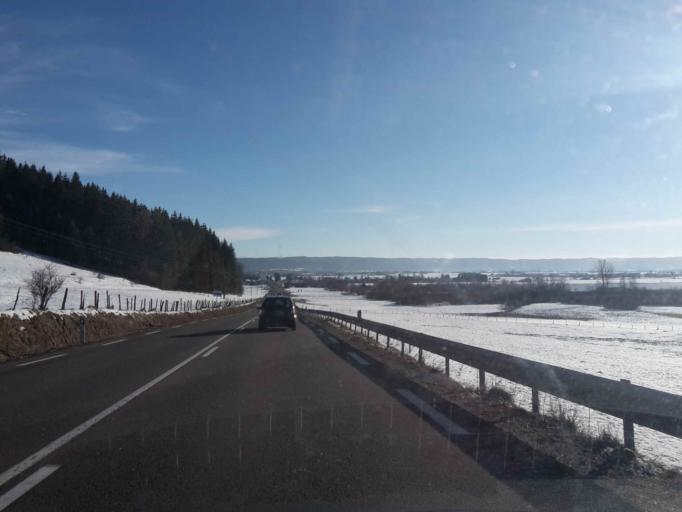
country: FR
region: Franche-Comte
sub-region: Departement du Doubs
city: Doubs
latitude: 46.9560
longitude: 6.3417
